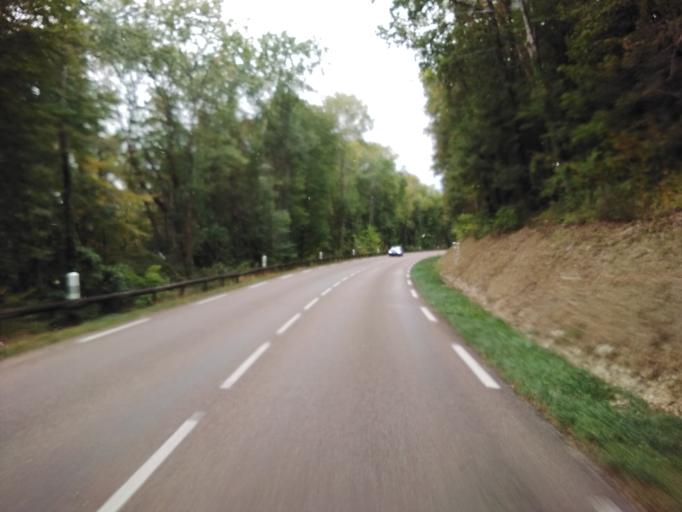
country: FR
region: Champagne-Ardenne
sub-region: Departement de l'Aube
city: Bar-sur-Seine
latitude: 48.1290
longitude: 4.3880
